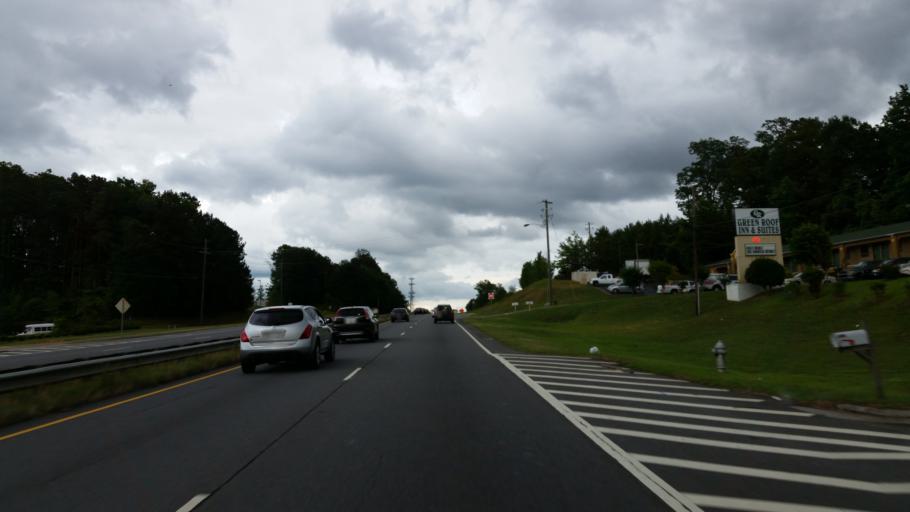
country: US
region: Georgia
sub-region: Cobb County
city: Kennesaw
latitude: 34.0281
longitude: -84.6440
